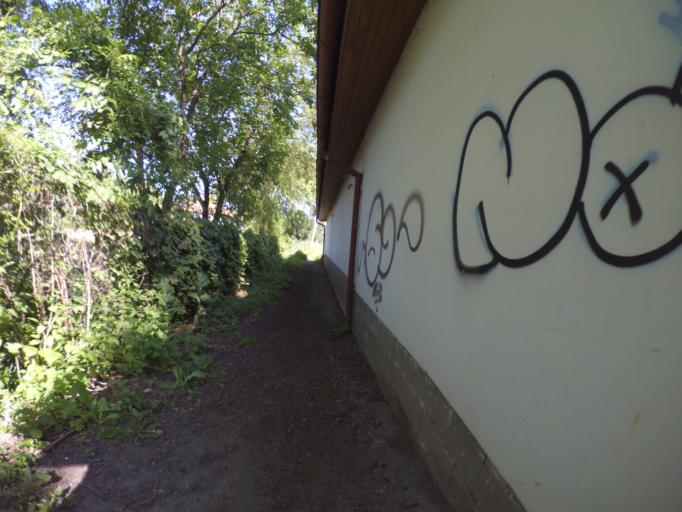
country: CZ
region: Central Bohemia
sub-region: Okres Nymburk
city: Podebrady
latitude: 50.1535
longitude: 15.1073
